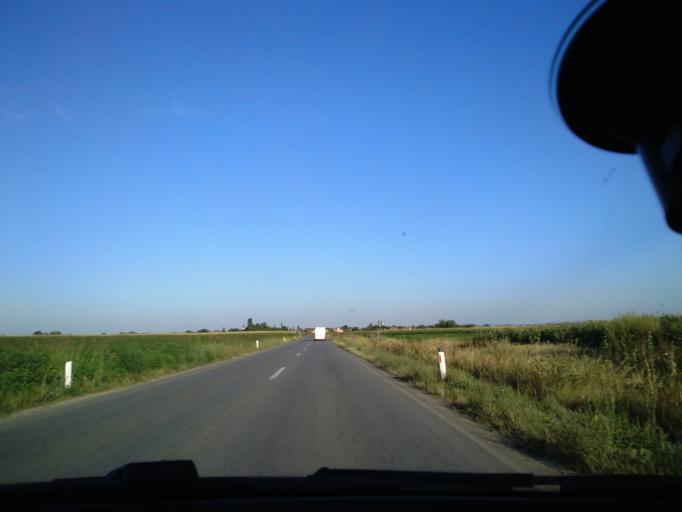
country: RS
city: Maglic
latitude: 45.4008
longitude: 19.4410
